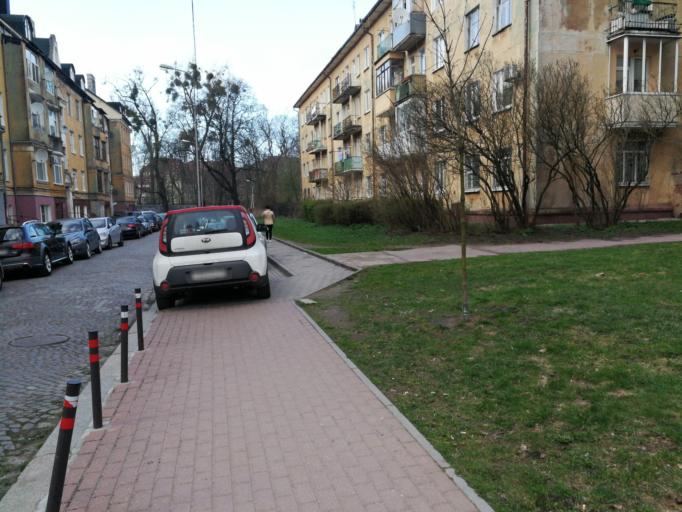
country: RU
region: Kaliningrad
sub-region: Gorod Kaliningrad
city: Kaliningrad
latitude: 54.7213
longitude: 20.4919
